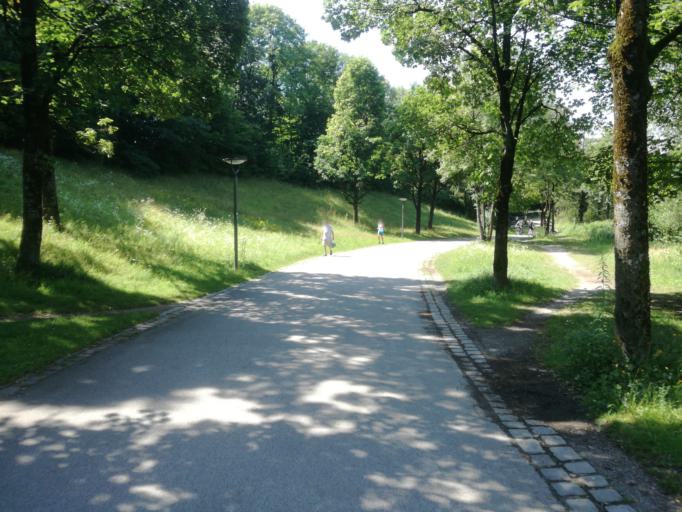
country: DE
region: Bavaria
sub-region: Upper Bavaria
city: Munich
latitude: 48.1241
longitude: 11.5279
